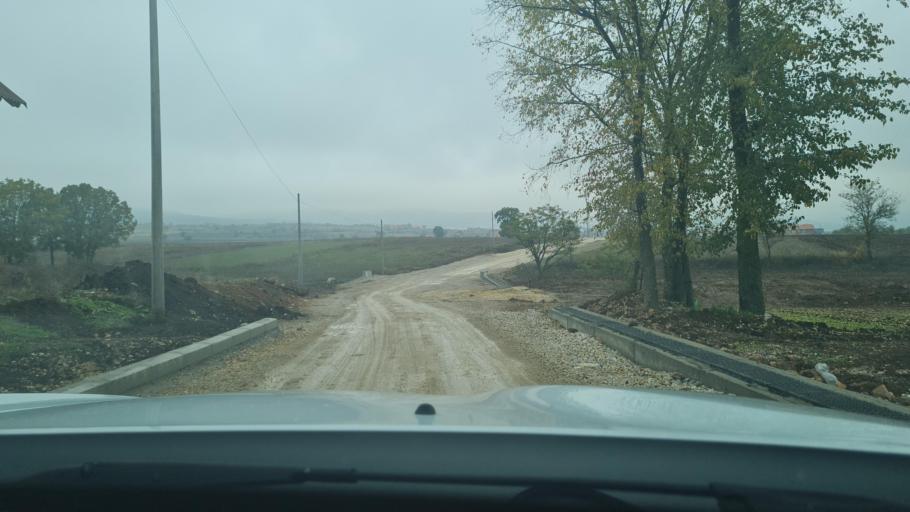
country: MK
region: Opstina Lipkovo
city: Matejche
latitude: 42.1133
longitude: 21.6114
